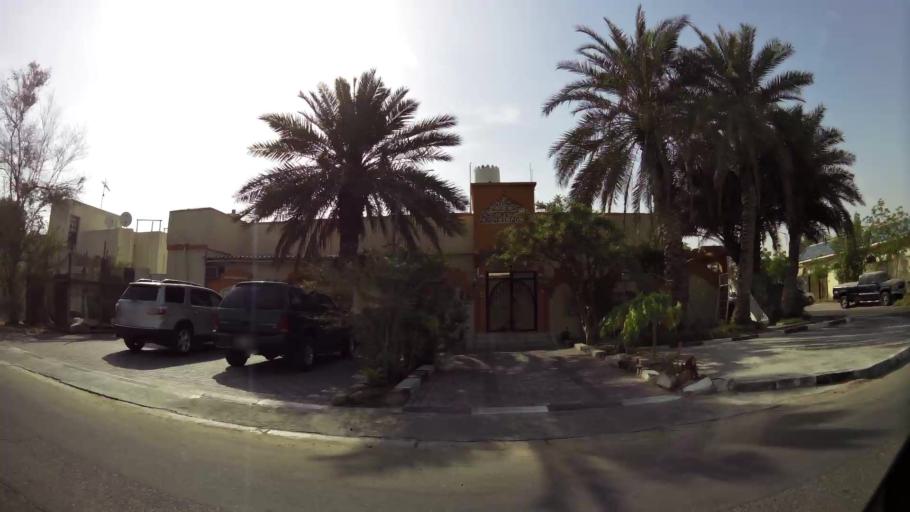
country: AE
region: Ash Shariqah
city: Sharjah
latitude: 25.2217
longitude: 55.3934
